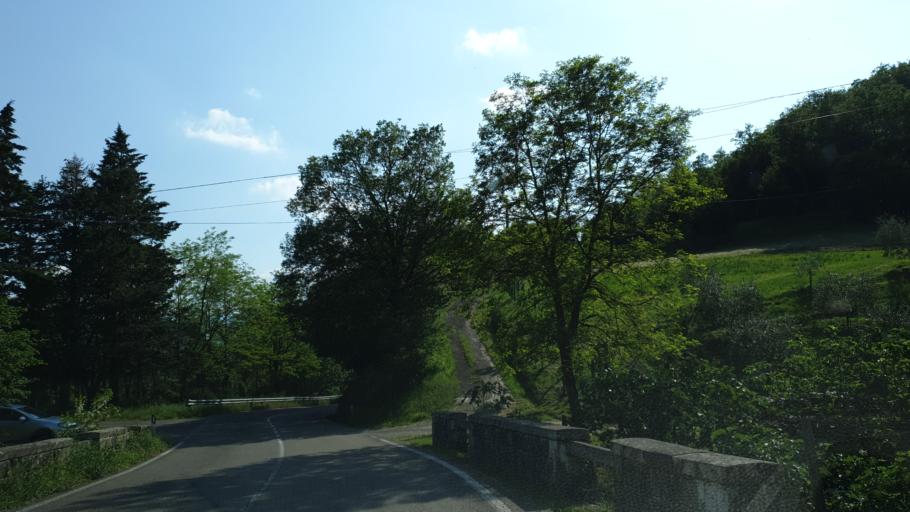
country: IT
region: Tuscany
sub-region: Province of Arezzo
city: Soci
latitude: 43.7615
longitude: 11.8349
